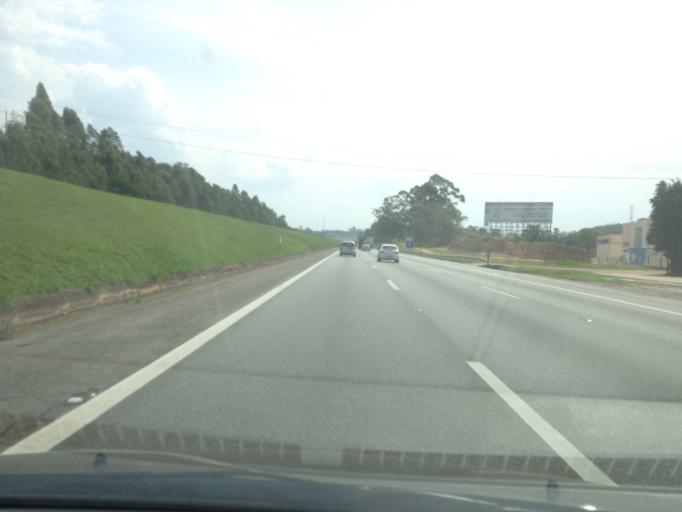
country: BR
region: Sao Paulo
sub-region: Mairinque
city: Mairinque
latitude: -23.4196
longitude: -47.2238
